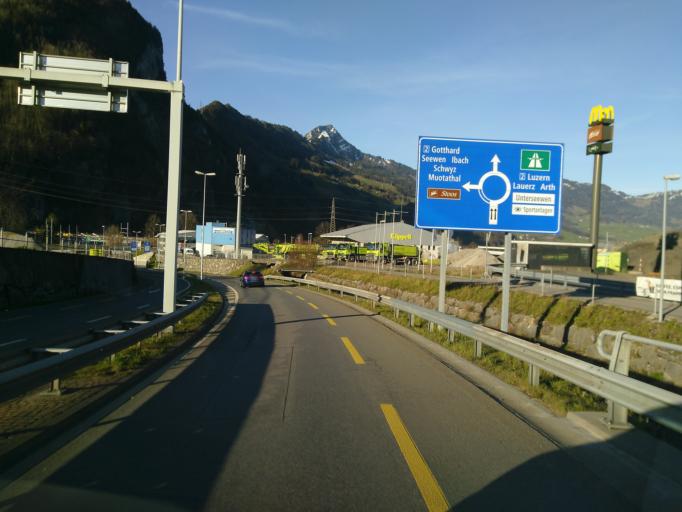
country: CH
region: Schwyz
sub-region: Bezirk Schwyz
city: Steinen
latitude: 47.0322
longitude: 8.6282
